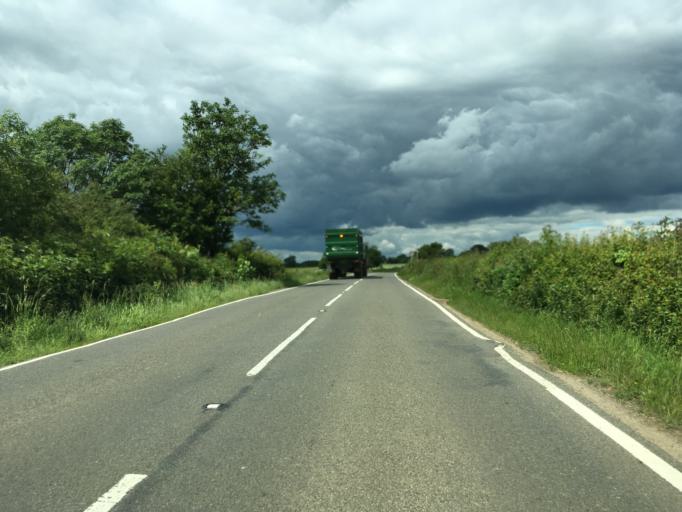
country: GB
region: England
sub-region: Northamptonshire
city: Brackley
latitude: 52.0886
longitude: -1.1992
